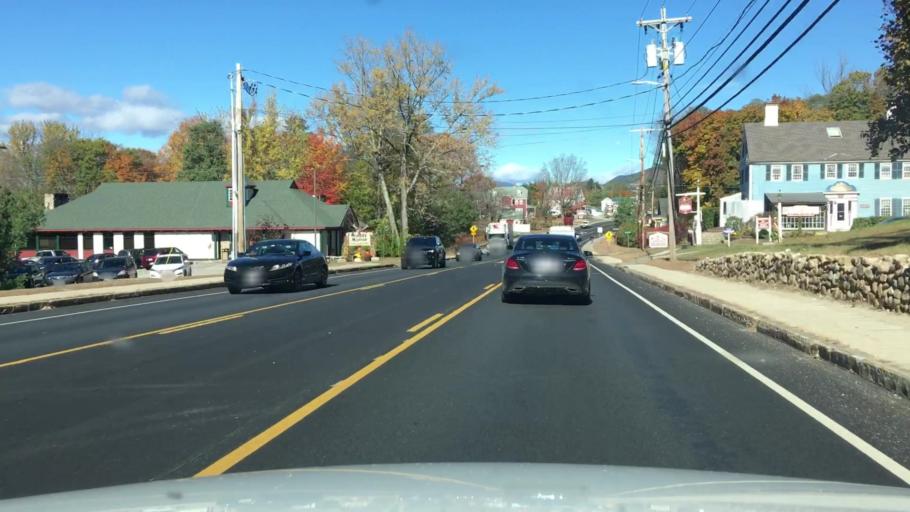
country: US
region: New Hampshire
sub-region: Carroll County
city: North Conway
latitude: 44.0433
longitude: -71.1246
